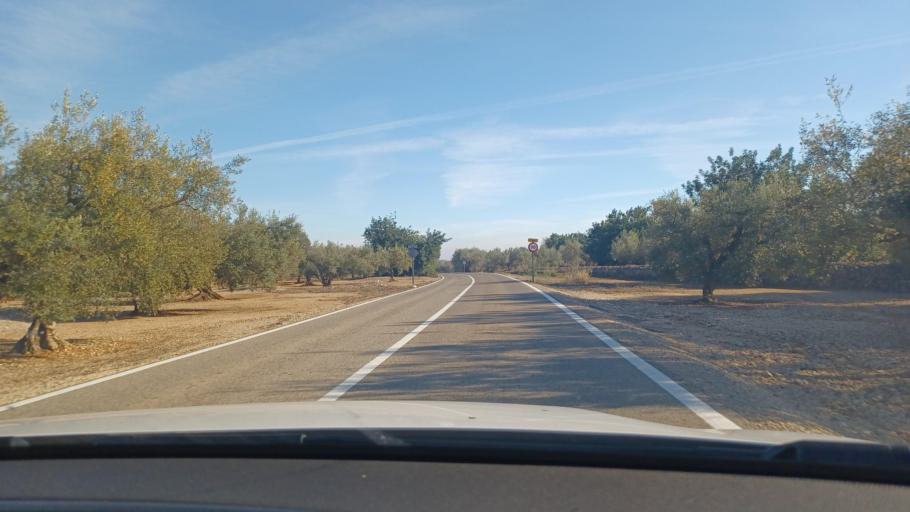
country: ES
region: Catalonia
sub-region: Provincia de Tarragona
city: Santa Barbara
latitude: 40.7201
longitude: 0.4542
